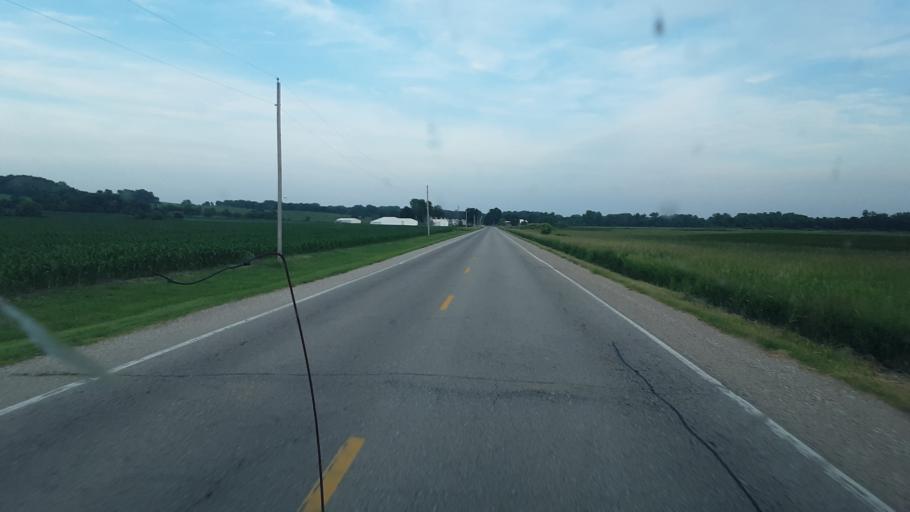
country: US
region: Iowa
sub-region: Benton County
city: Belle Plaine
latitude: 41.9400
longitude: -92.4116
